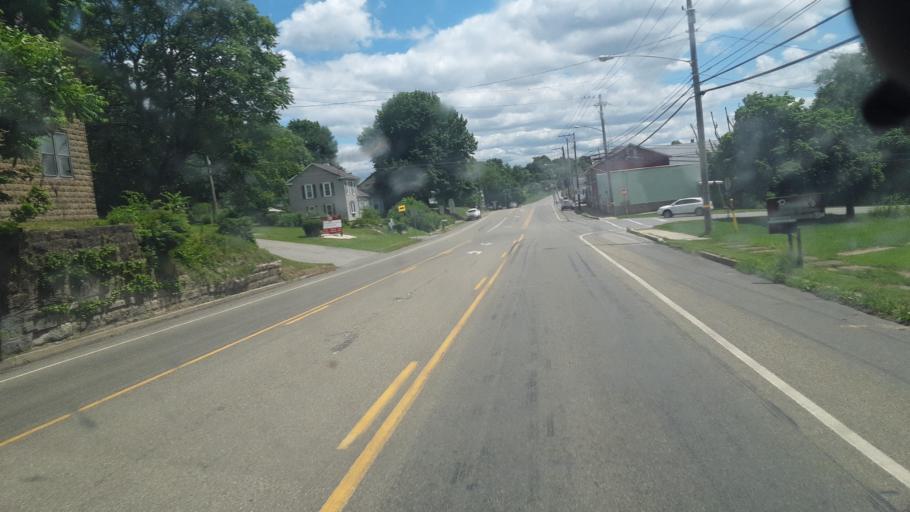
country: US
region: Pennsylvania
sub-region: Butler County
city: Prospect
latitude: 40.9259
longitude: -80.1442
